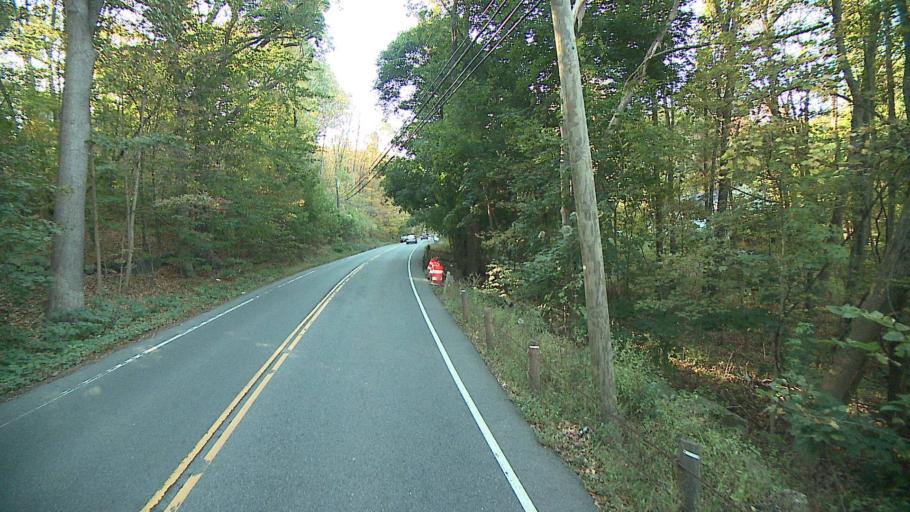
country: US
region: Connecticut
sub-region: Fairfield County
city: Bethel
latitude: 41.3527
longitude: -73.4143
